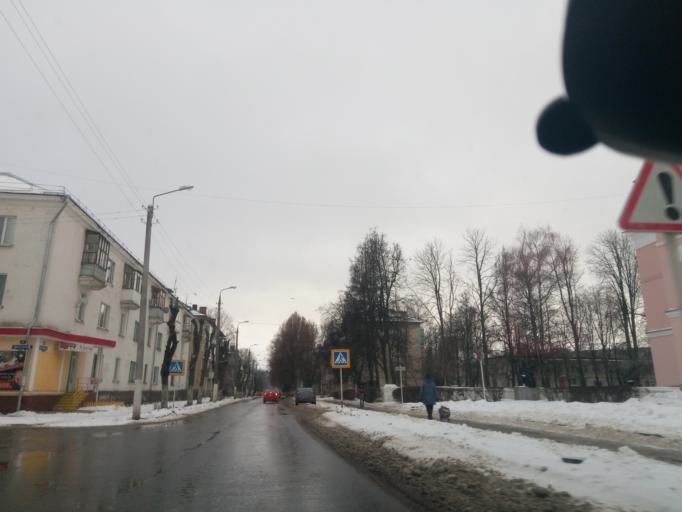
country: RU
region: Tula
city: Novomoskovsk
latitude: 54.0075
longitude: 38.2852
